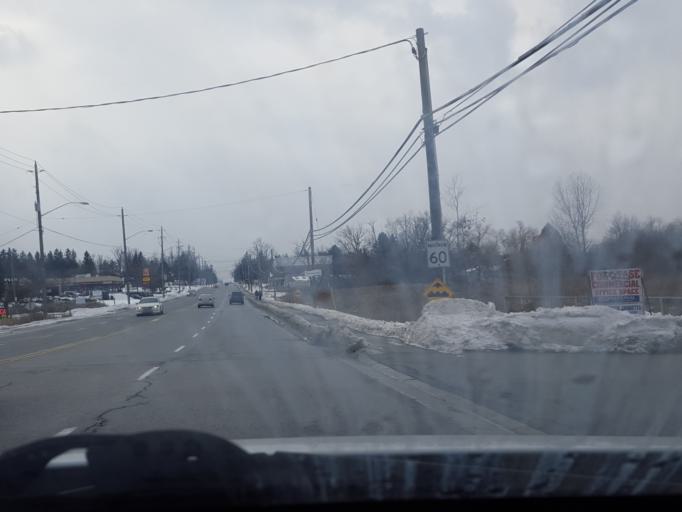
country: CA
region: Ontario
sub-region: York
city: Richmond Hill
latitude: 43.9444
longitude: -79.4562
